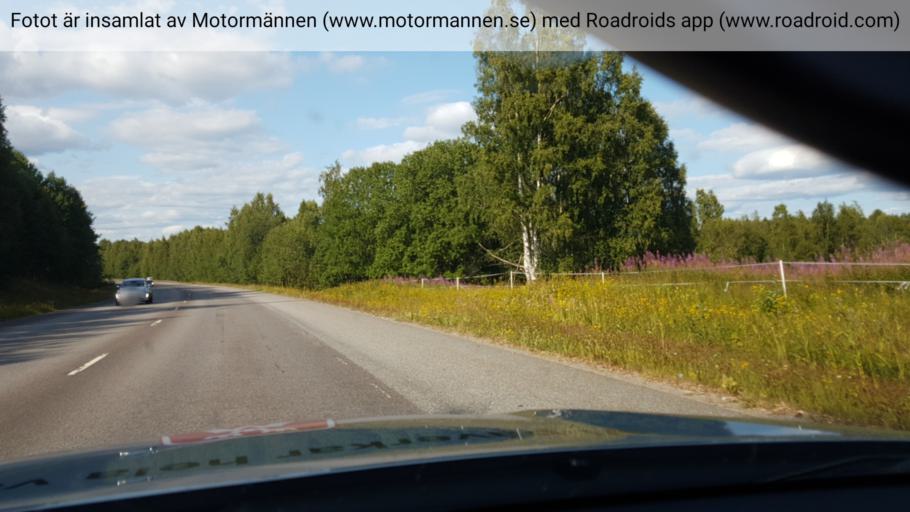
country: SE
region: Norrbotten
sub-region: Pitea Kommun
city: Pitea
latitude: 65.3025
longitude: 21.5102
